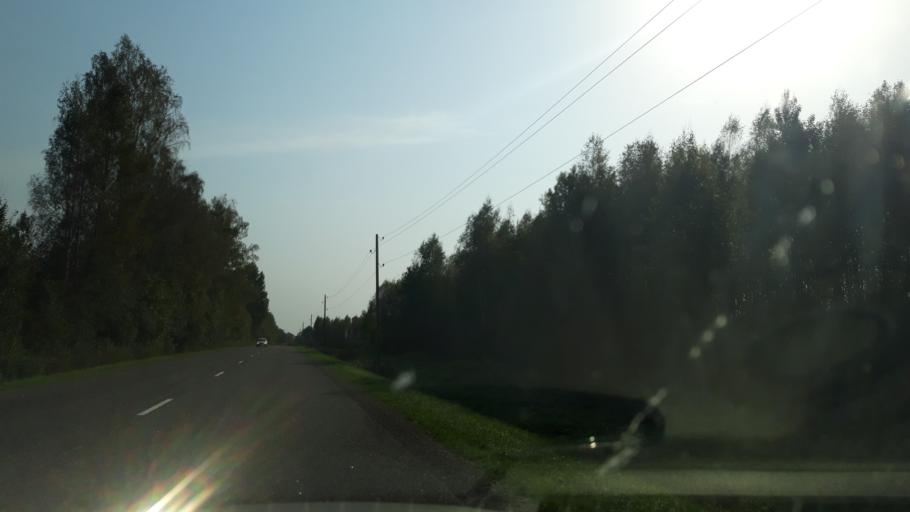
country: LV
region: Burtnieki
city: Matisi
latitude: 57.6338
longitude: 25.2585
